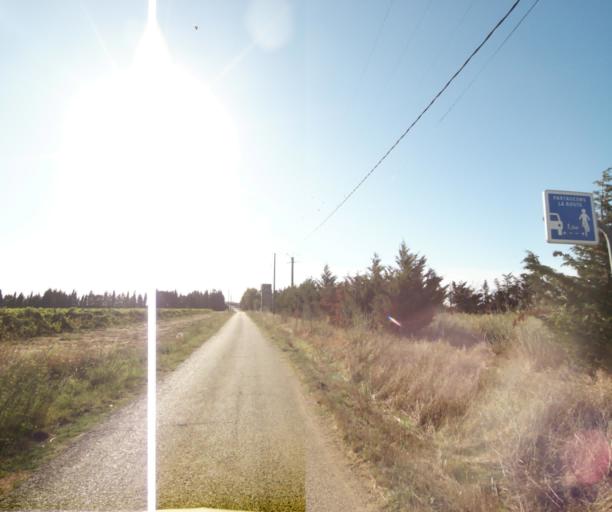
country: FR
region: Languedoc-Roussillon
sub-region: Departement du Gard
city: Bouillargues
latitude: 43.7925
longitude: 4.4514
